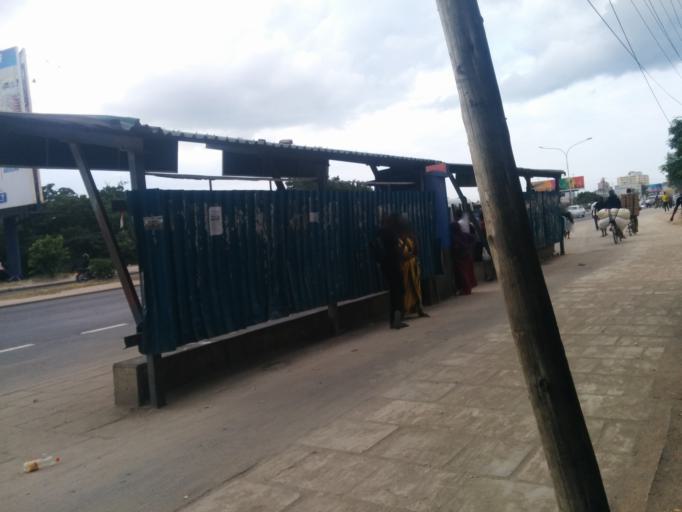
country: TZ
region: Dar es Salaam
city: Dar es Salaam
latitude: -6.8309
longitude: 39.2709
